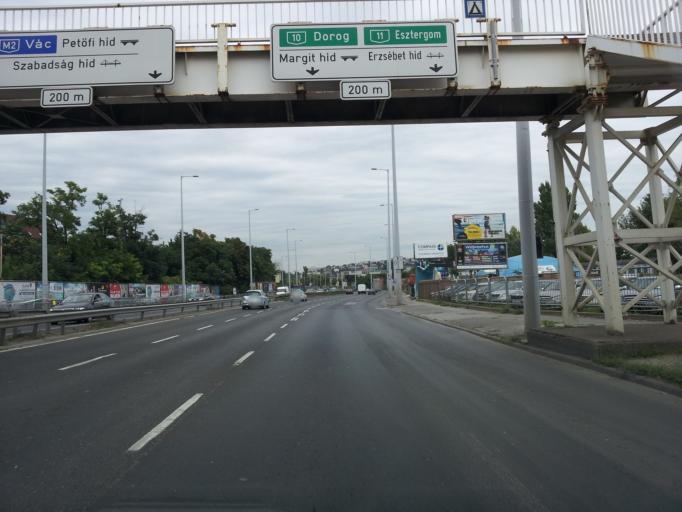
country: HU
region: Budapest
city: Budapest XI. keruelet
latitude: 47.4708
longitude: 19.0202
